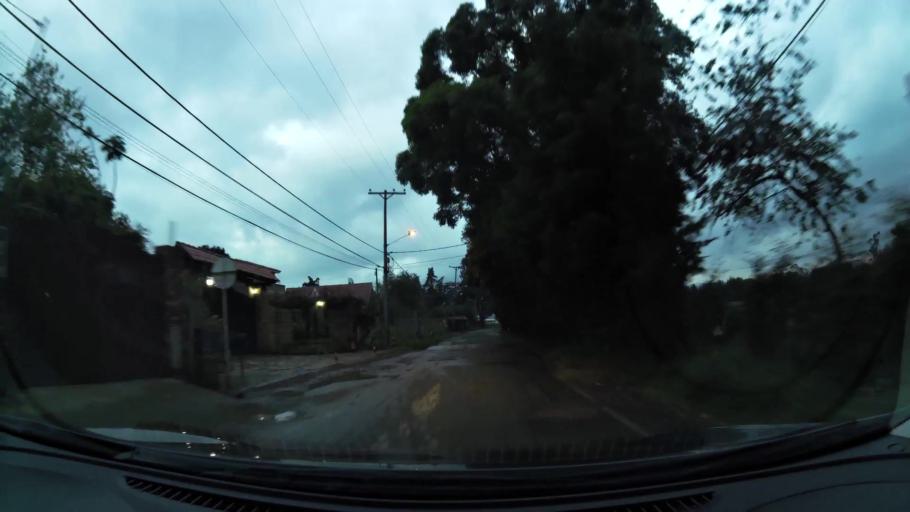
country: CO
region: Cundinamarca
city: Chia
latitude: 4.8373
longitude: -74.0712
